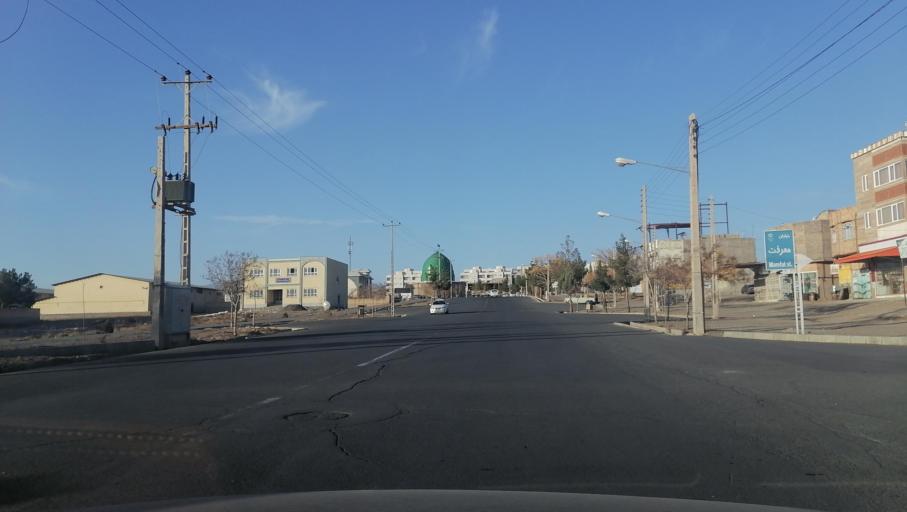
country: IR
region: Razavi Khorasan
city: Sabzevar
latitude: 36.2827
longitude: 57.6751
